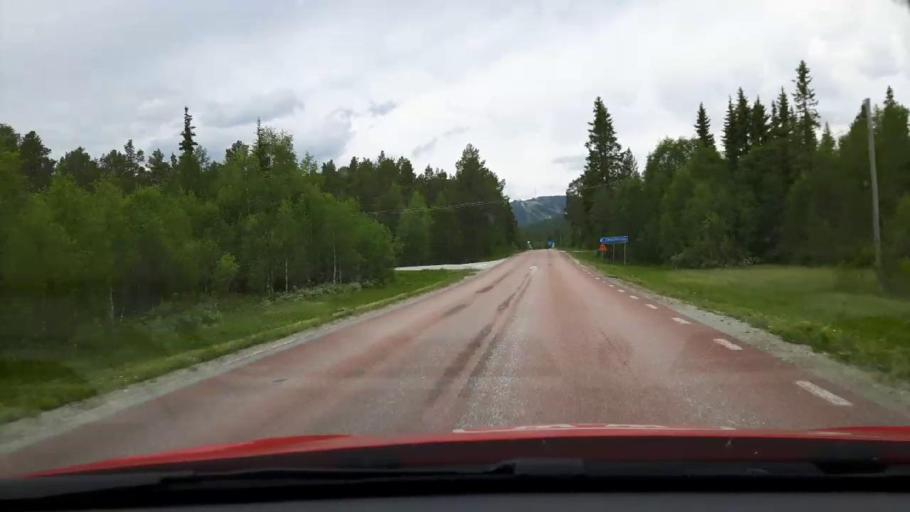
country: NO
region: Hedmark
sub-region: Engerdal
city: Engerdal
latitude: 62.5182
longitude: 12.5977
